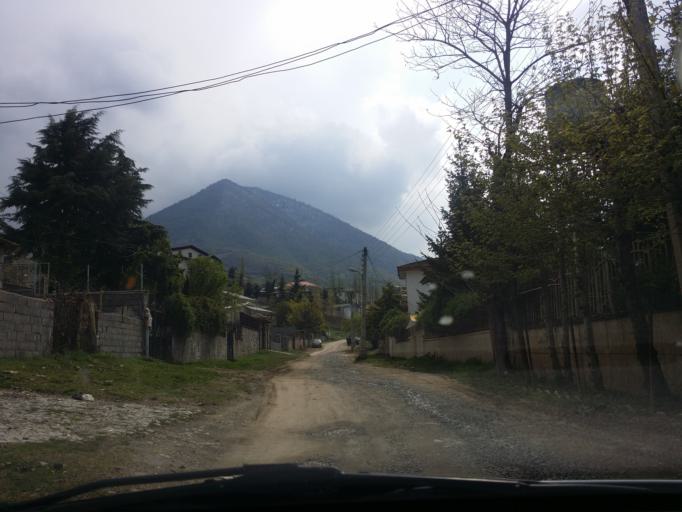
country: IR
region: Mazandaran
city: `Abbasabad
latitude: 36.4879
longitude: 51.1440
